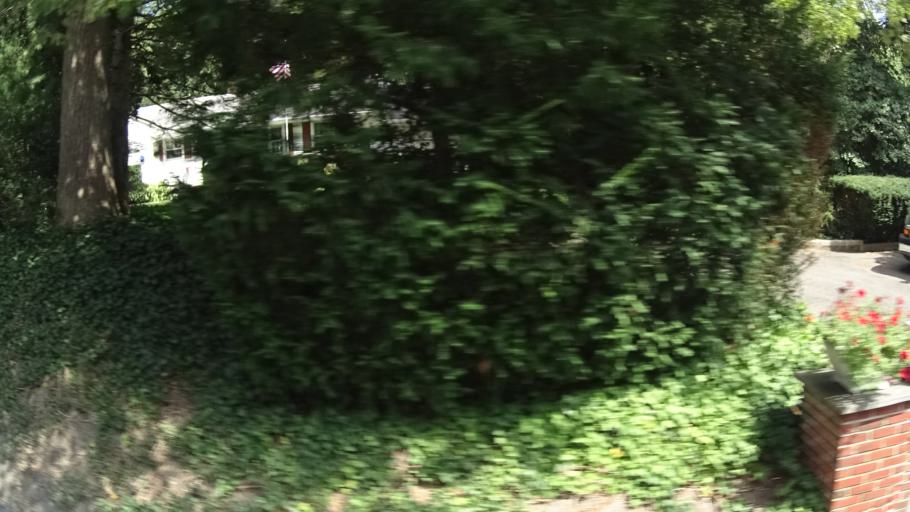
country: US
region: New Jersey
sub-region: Monmouth County
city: Brielle
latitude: 40.1154
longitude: -74.0858
